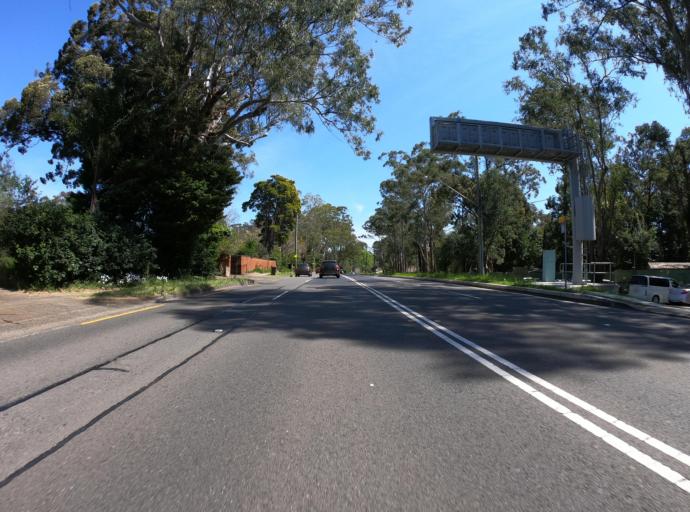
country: AU
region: New South Wales
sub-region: The Hills Shire
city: West Pennant
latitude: -33.7424
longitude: 151.0445
